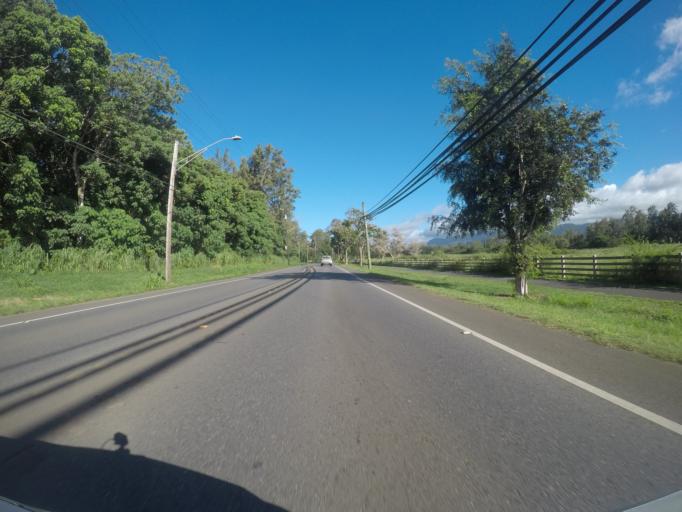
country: US
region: Hawaii
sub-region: Honolulu County
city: La'ie
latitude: 21.6583
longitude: -157.9320
